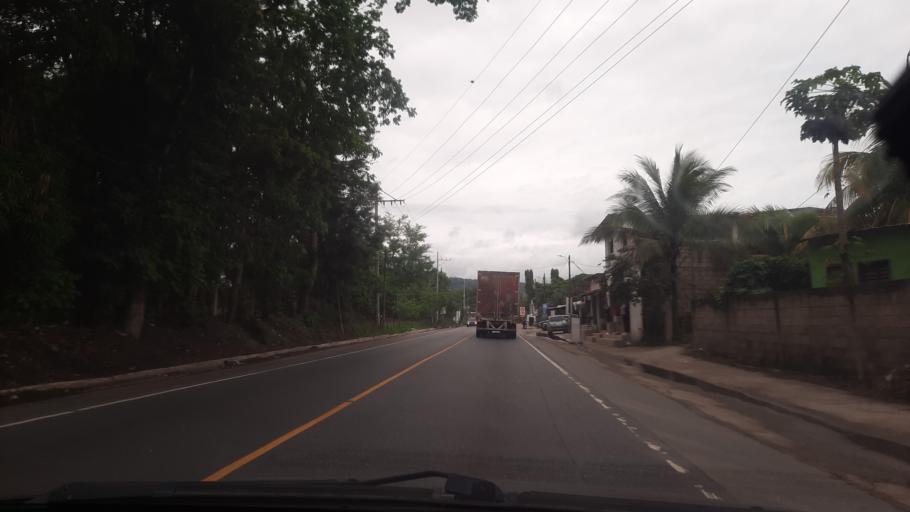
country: GT
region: Izabal
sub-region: Municipio de Los Amates
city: Los Amates
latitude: 15.2614
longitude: -89.0884
